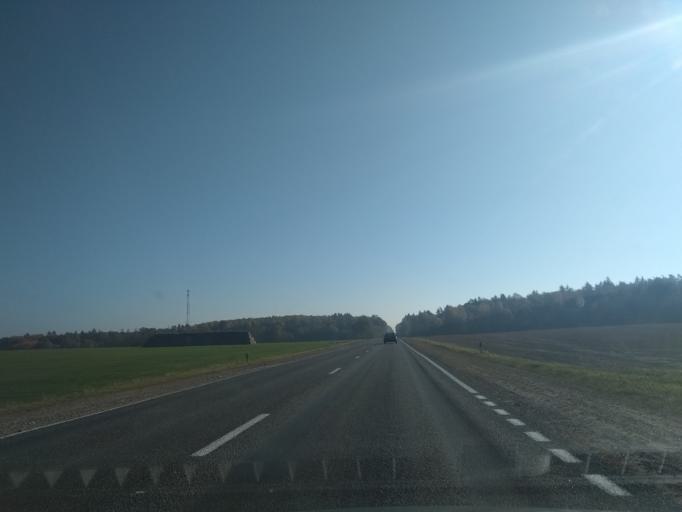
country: BY
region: Grodnenskaya
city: Slonim
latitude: 53.1130
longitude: 25.1571
